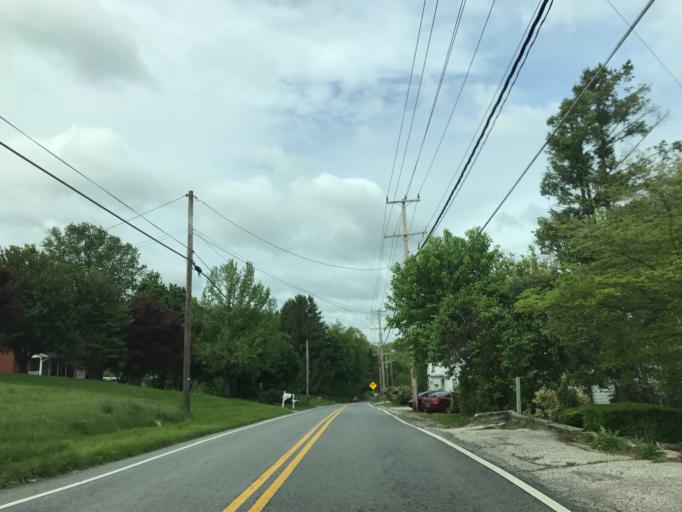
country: US
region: Maryland
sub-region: Baltimore County
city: Reisterstown
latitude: 39.4921
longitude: -76.8918
